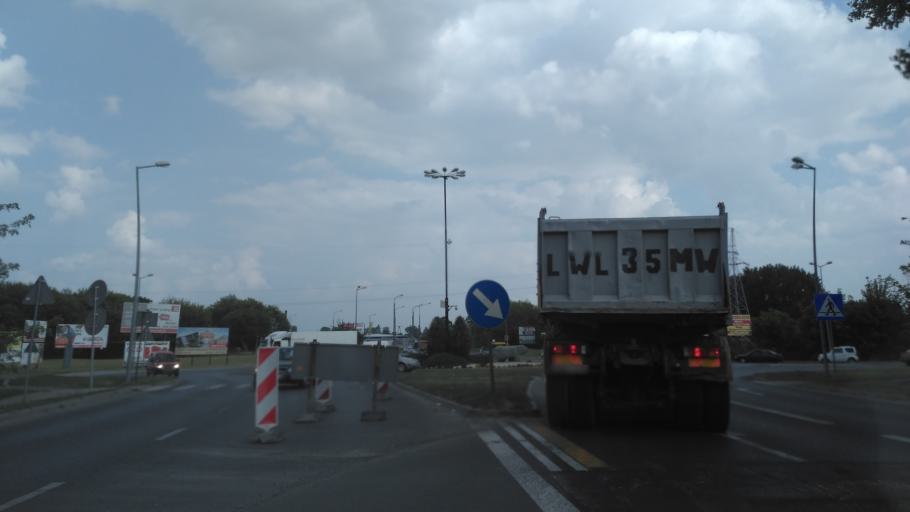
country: PL
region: Lublin Voivodeship
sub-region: Chelm
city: Chelm
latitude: 51.1434
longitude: 23.4704
